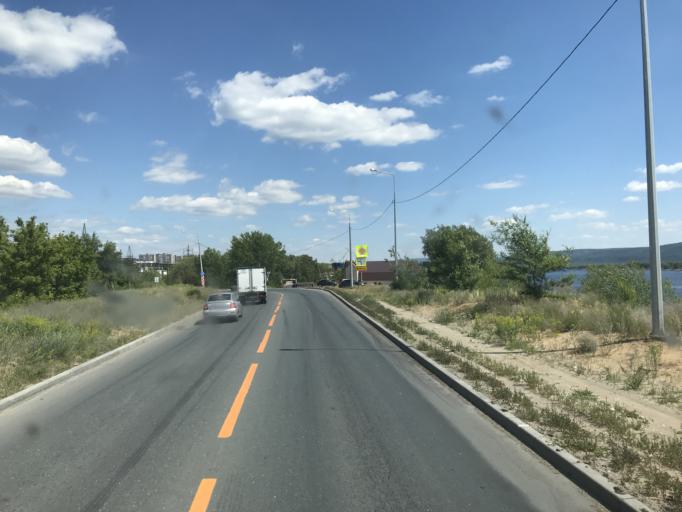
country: RU
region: Samara
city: Zhigulevsk
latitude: 53.4677
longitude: 49.5111
